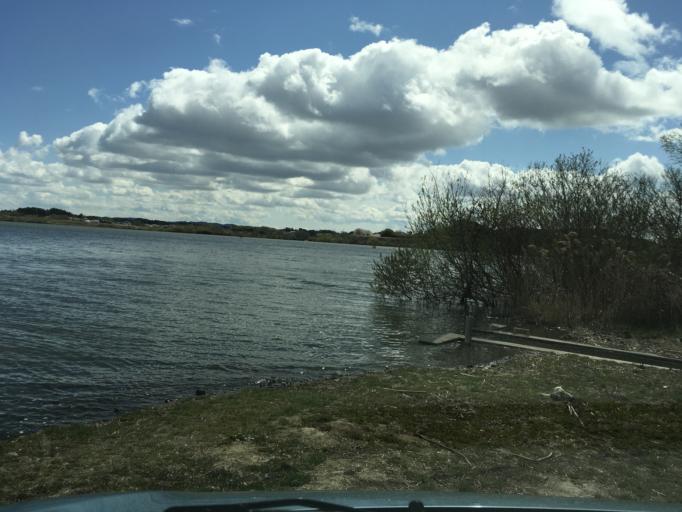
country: JP
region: Miyagi
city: Wakuya
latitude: 38.6932
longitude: 141.1214
